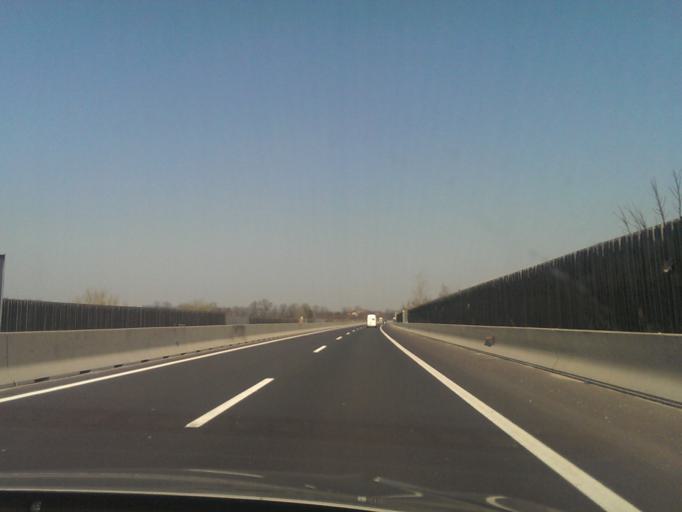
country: AT
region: Upper Austria
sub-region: Politischer Bezirk Kirchdorf an der Krems
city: Micheldorf in Oberoesterreich
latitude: 47.9083
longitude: 14.1010
